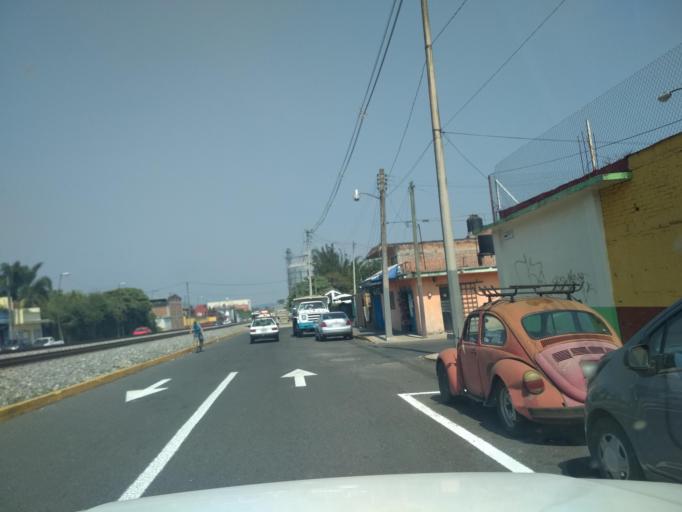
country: MX
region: Veracruz
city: Orizaba
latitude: 18.8450
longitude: -97.0919
